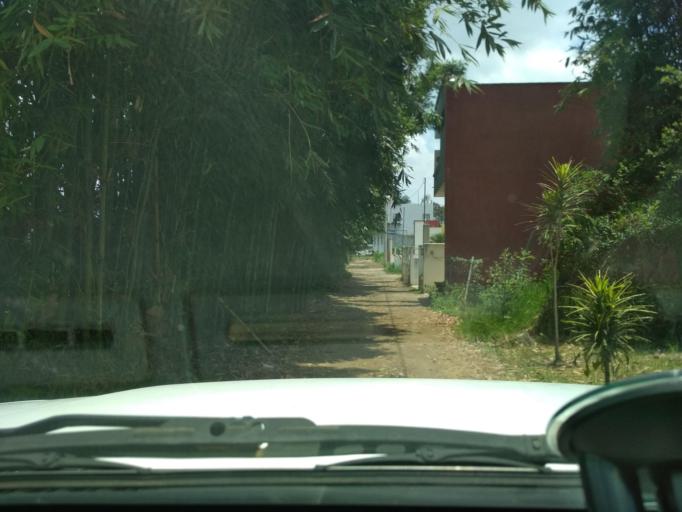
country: MX
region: Veracruz
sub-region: Cordoba
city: San Jose de Abajo [Unidad Habitacional]
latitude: 18.9107
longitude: -96.9585
